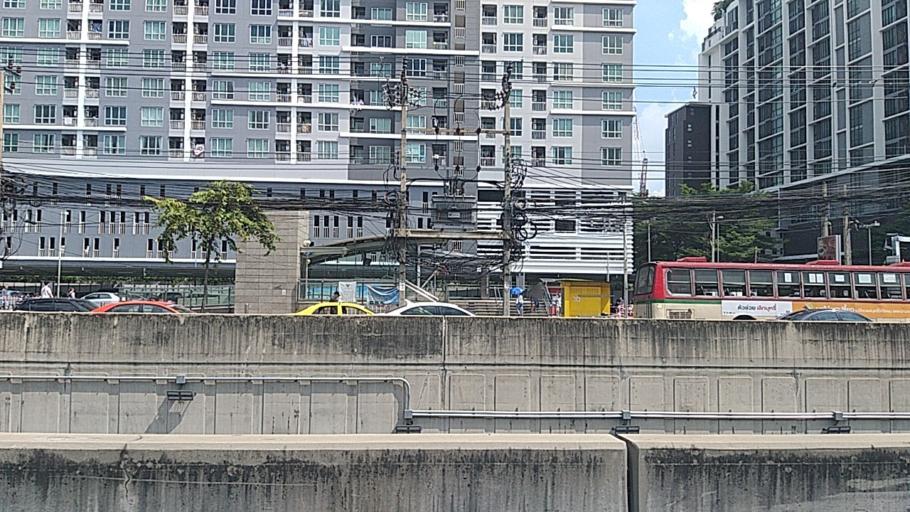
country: TH
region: Bangkok
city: Huai Khwang
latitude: 13.7790
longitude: 100.5738
